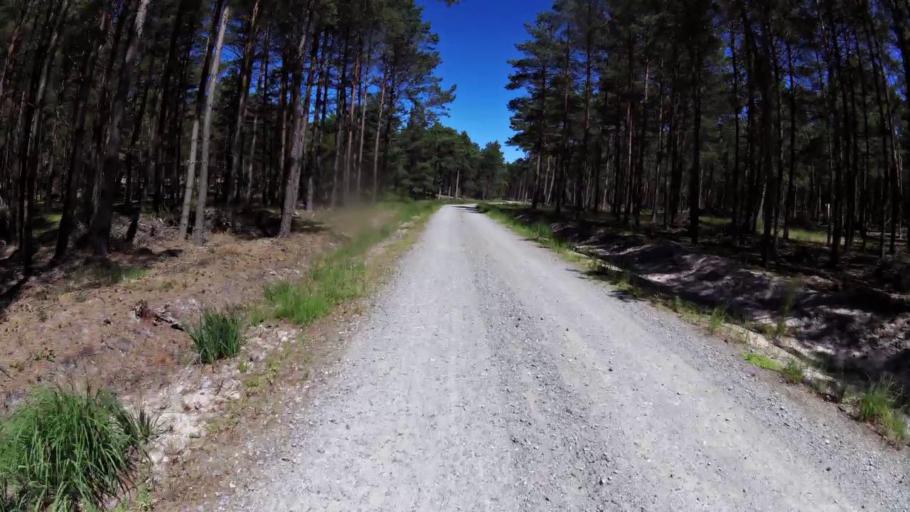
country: PL
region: West Pomeranian Voivodeship
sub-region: Powiat gryficki
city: Trzebiatow
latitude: 54.1167
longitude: 15.2015
